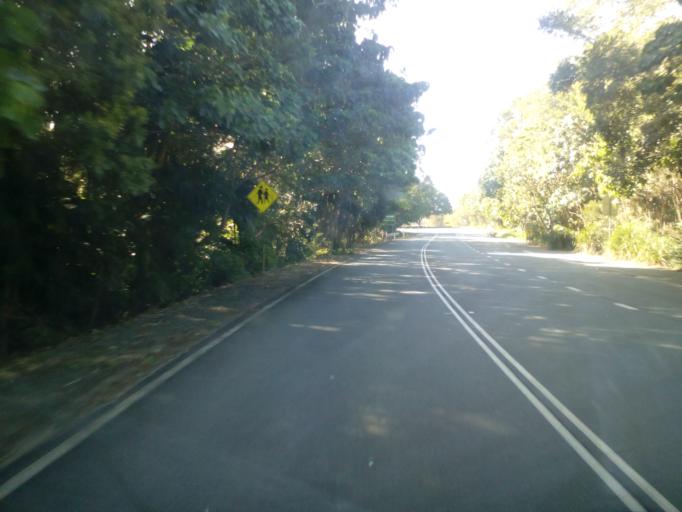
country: AU
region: New South Wales
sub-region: Tweed
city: Kingscliff
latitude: -28.2603
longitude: 153.5705
